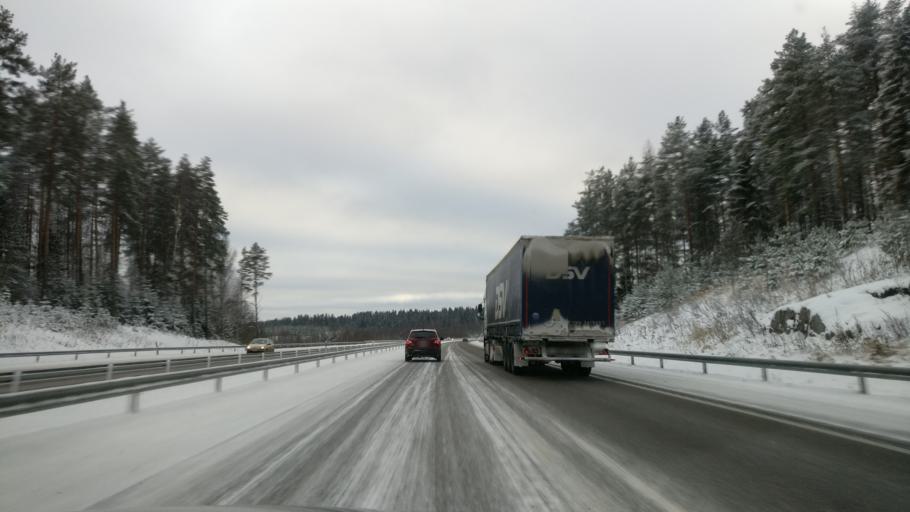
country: FI
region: Paijanne Tavastia
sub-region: Lahti
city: Nastola
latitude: 61.0100
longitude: 25.8167
